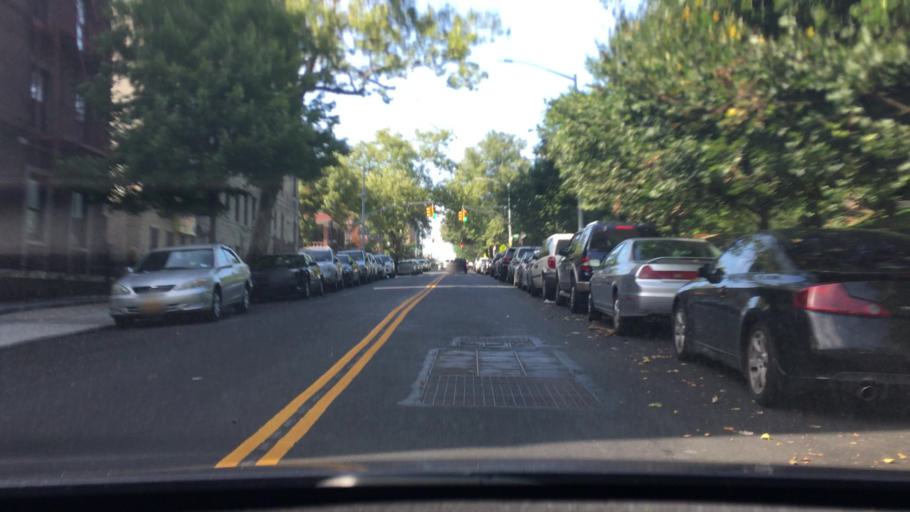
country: US
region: New York
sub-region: Kings County
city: Brooklyn
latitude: 40.6670
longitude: -73.9286
